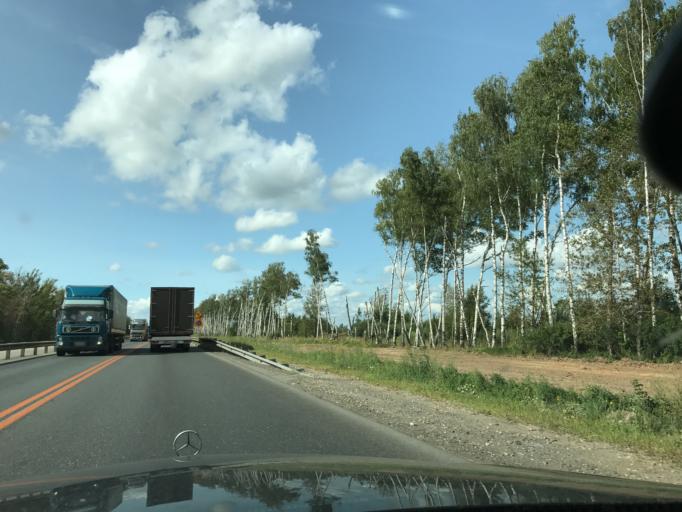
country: RU
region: Vladimir
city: Novovyazniki
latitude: 56.2100
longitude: 42.2704
